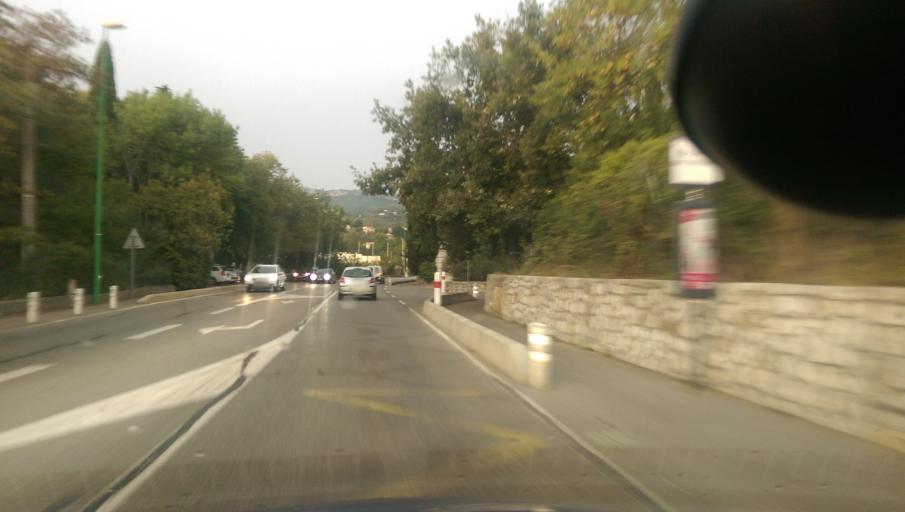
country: FR
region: Provence-Alpes-Cote d'Azur
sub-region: Departement des Alpes-Maritimes
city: Chateauneuf-Grasse
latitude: 43.6630
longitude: 6.9870
